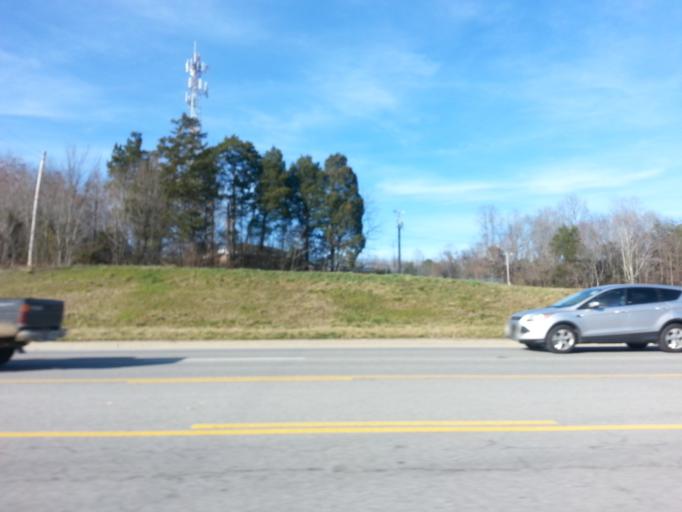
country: US
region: Tennessee
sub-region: Warren County
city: McMinnville
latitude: 35.6996
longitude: -85.8227
